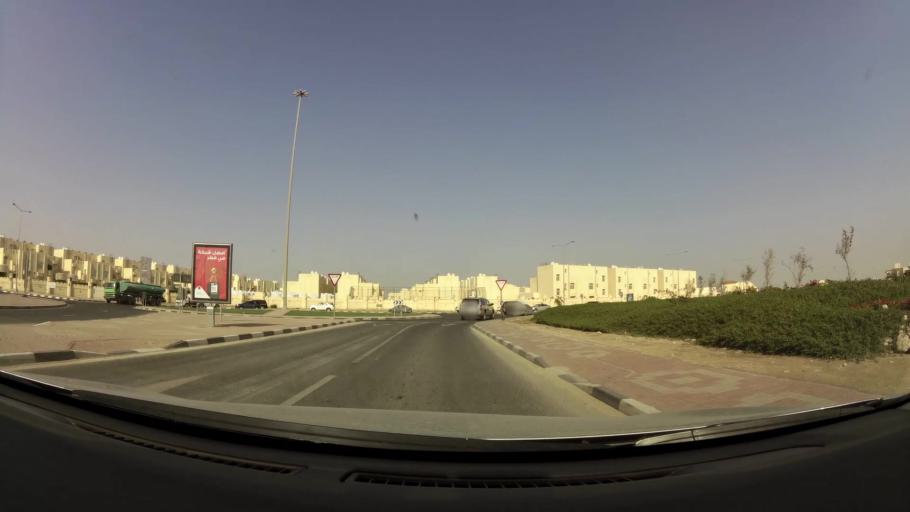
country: QA
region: Baladiyat ar Rayyan
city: Ar Rayyan
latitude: 25.3452
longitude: 51.4461
